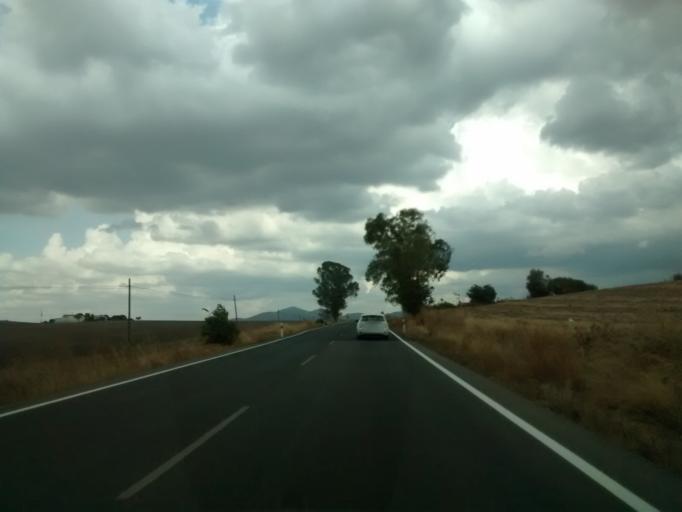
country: ES
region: Andalusia
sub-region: Provincia de Cadiz
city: Villamartin
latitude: 36.8669
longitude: -5.6035
